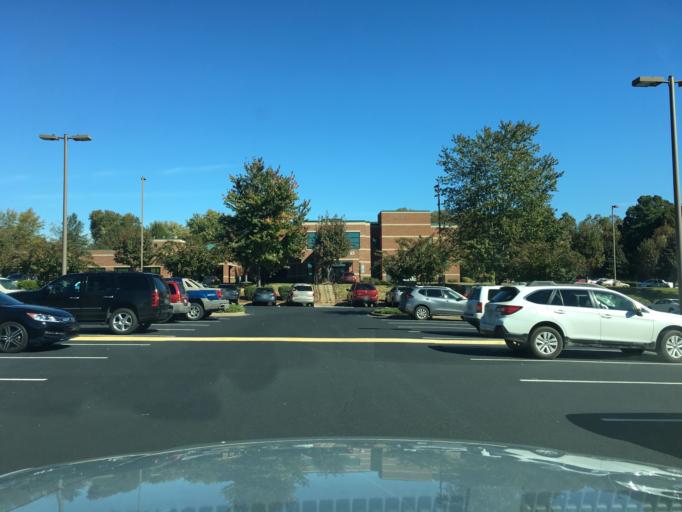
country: US
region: North Carolina
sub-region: Catawba County
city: Hickory
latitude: 35.7310
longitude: -81.3100
